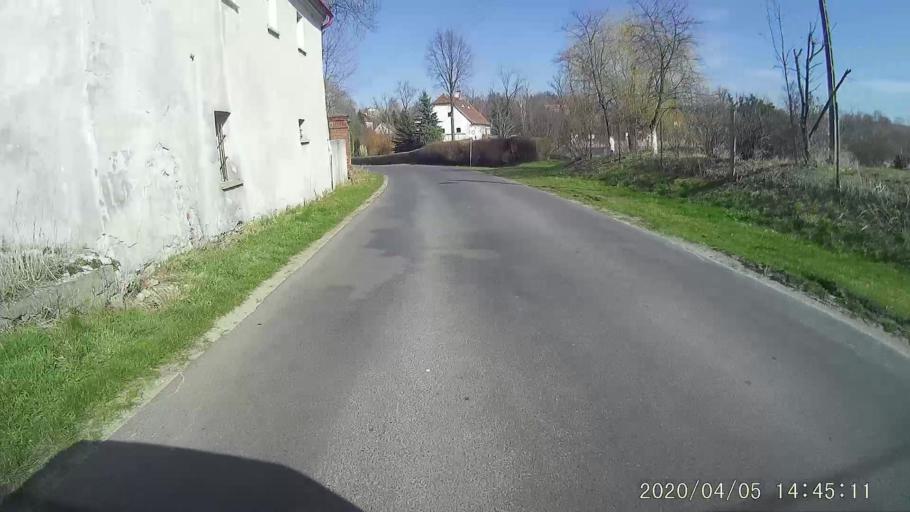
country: PL
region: Lower Silesian Voivodeship
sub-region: Powiat zgorzelecki
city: Sulikow
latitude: 51.0534
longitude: 15.1108
